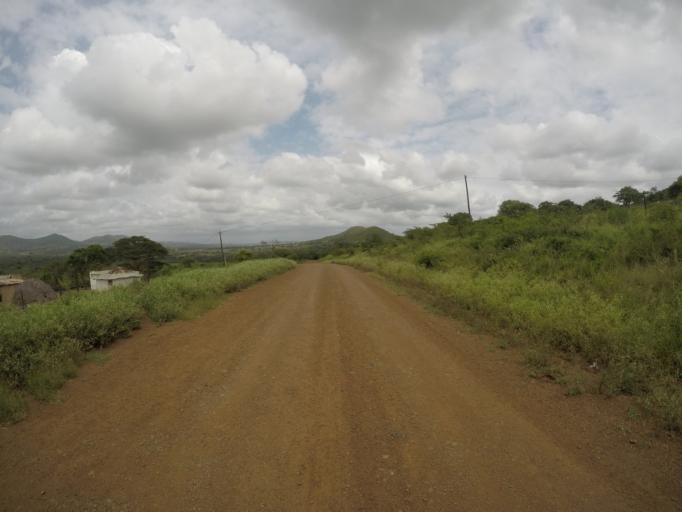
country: ZA
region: KwaZulu-Natal
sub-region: uThungulu District Municipality
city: Empangeni
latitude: -28.5947
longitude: 31.8795
